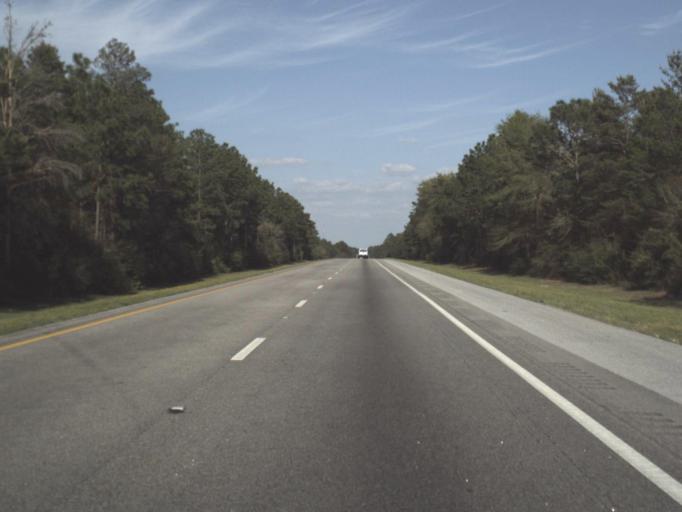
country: US
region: Florida
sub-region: Okaloosa County
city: Crestview
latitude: 30.7267
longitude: -86.3996
